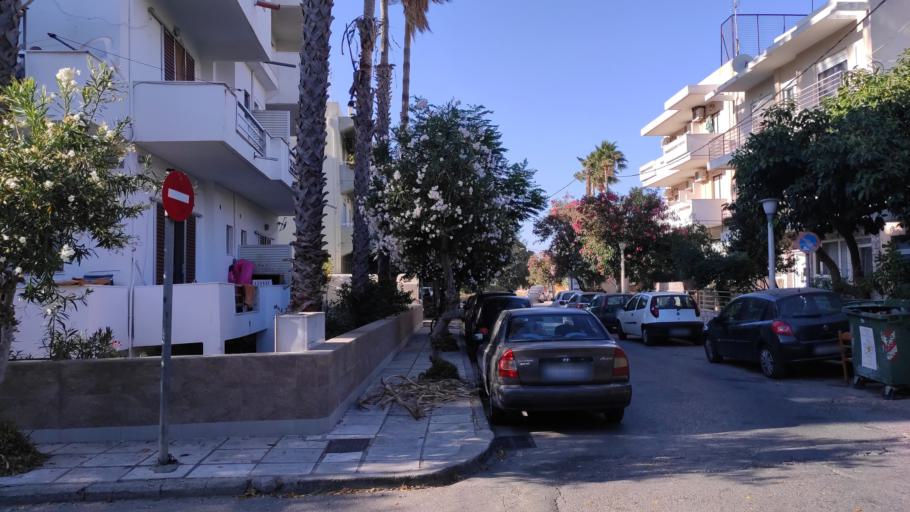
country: GR
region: South Aegean
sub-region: Nomos Dodekanisou
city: Kos
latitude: 36.8958
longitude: 27.2831
